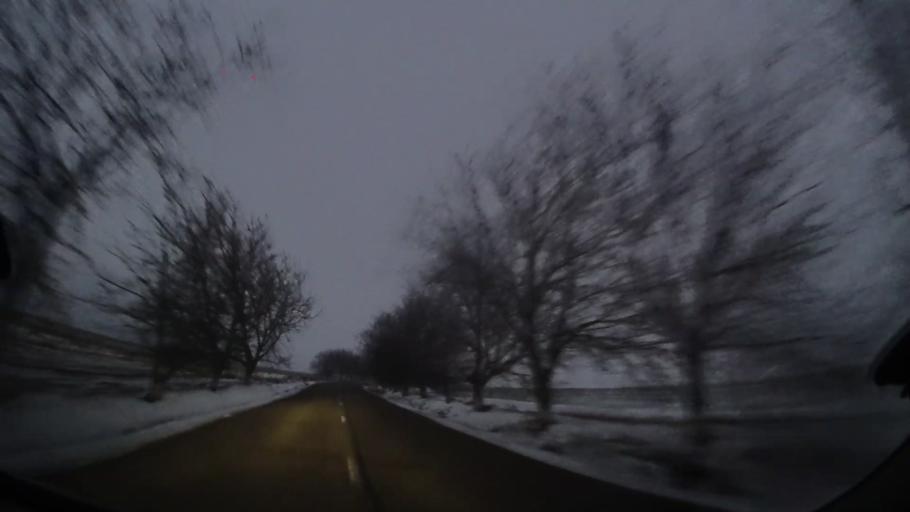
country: RO
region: Vaslui
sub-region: Comuna Dimitrie Cantemir
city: Dimitrie Cantemir
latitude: 46.5135
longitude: 28.0323
